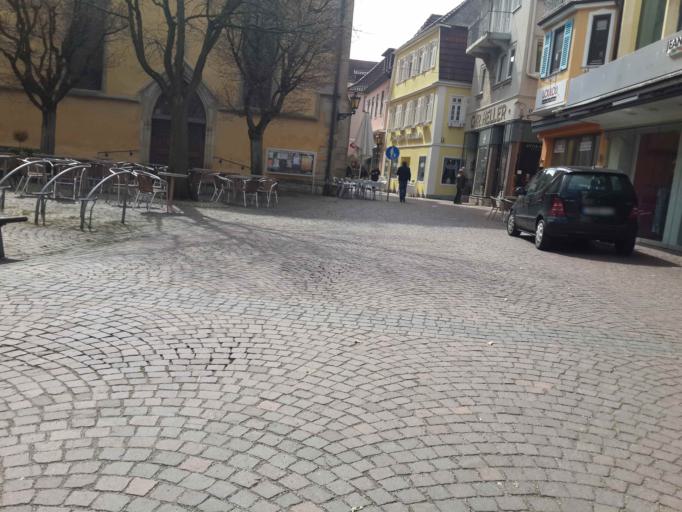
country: DE
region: Baden-Wuerttemberg
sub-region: Regierungsbezirk Stuttgart
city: Bad Mergentheim
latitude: 49.4918
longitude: 9.7728
